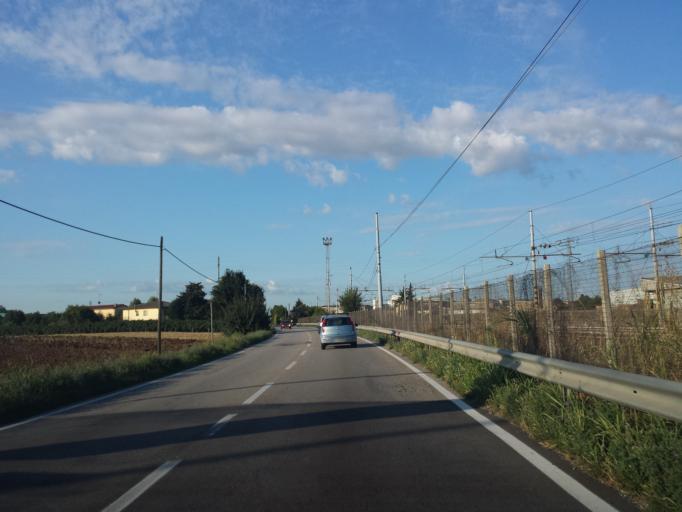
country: IT
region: Veneto
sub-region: Provincia di Vicenza
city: Tavernelle
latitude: 45.5100
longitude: 11.4528
